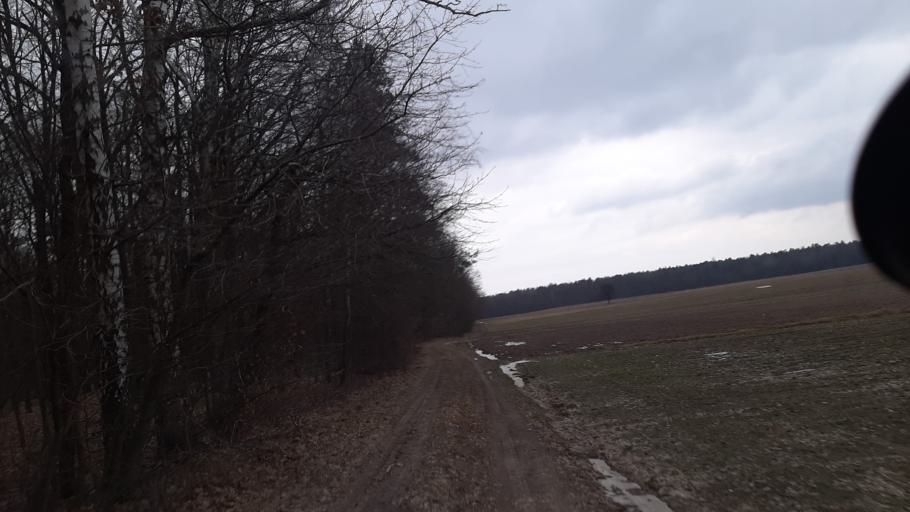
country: PL
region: Lublin Voivodeship
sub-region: Powiat lubelski
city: Garbow
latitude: 51.3887
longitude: 22.4036
